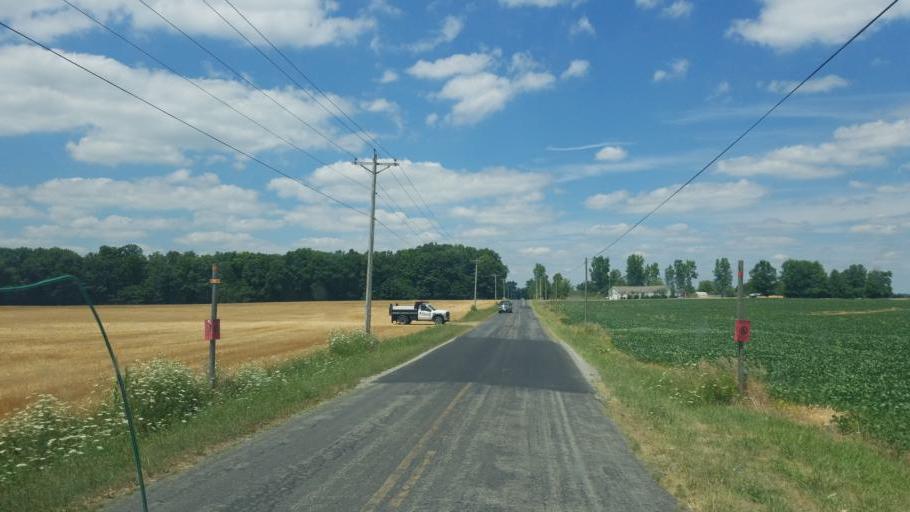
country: US
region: Ohio
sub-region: Williams County
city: Edgerton
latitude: 41.4418
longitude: -84.7103
